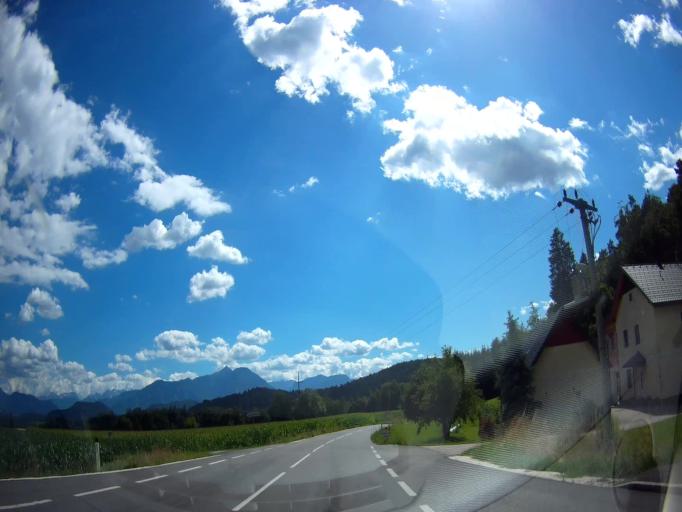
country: AT
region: Carinthia
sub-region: Politischer Bezirk Volkermarkt
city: Voelkermarkt
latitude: 46.6533
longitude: 14.5535
